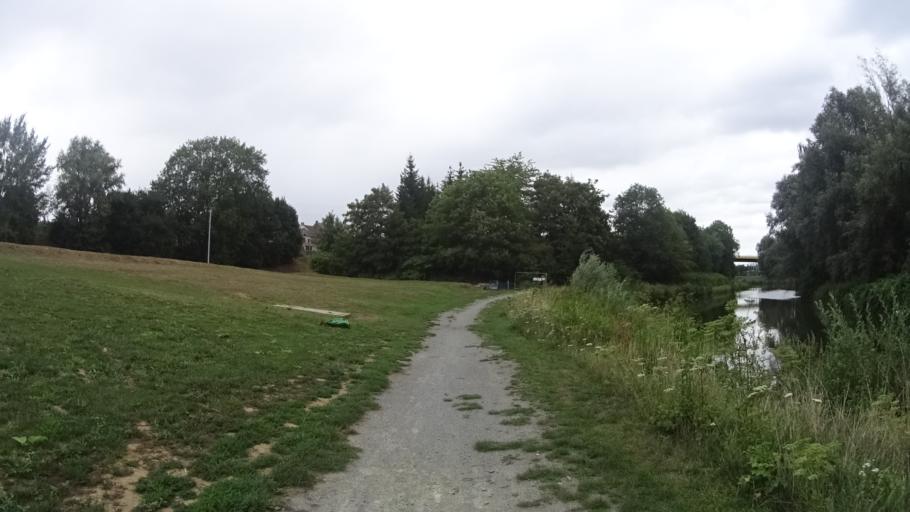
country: FR
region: Nord-Pas-de-Calais
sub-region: Departement du Nord
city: Hautmont
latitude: 50.2604
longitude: 3.9219
